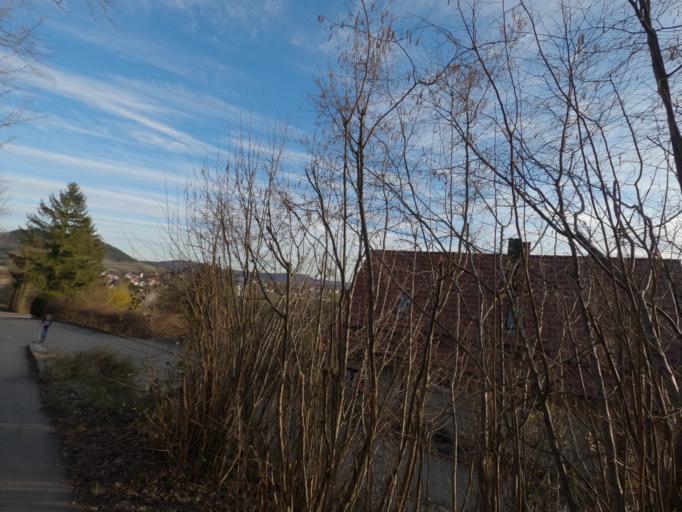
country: DE
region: Baden-Wuerttemberg
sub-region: Regierungsbezirk Stuttgart
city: Waldstetten
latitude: 48.7551
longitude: 9.7869
